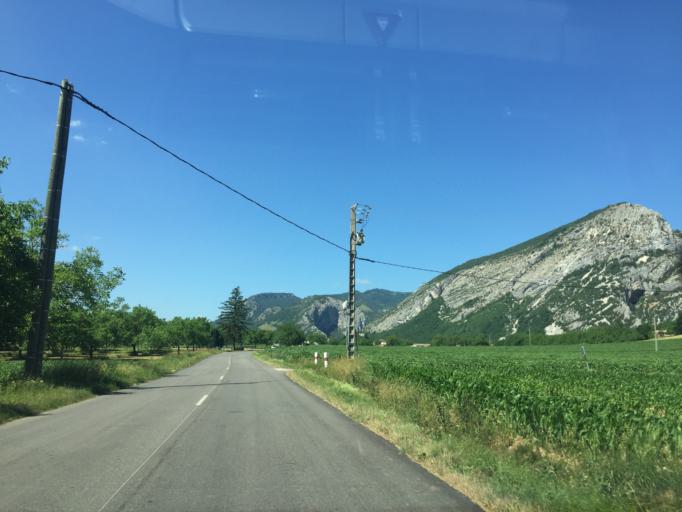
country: FR
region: Rhone-Alpes
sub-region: Departement de la Drome
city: Saint-Laurent-en-Royans
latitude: 45.0402
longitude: 5.3371
